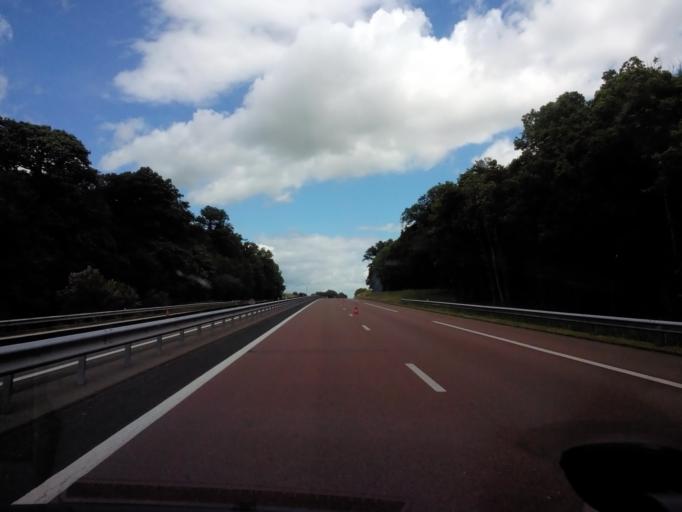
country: FR
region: Champagne-Ardenne
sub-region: Departement de la Haute-Marne
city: Saulxures
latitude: 48.0628
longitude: 5.5872
